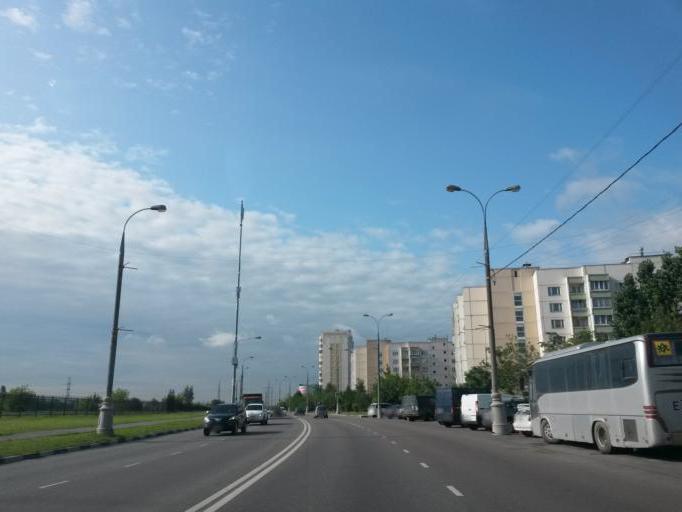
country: RU
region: Moscow
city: Brateyevo
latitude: 55.6582
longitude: 37.7781
